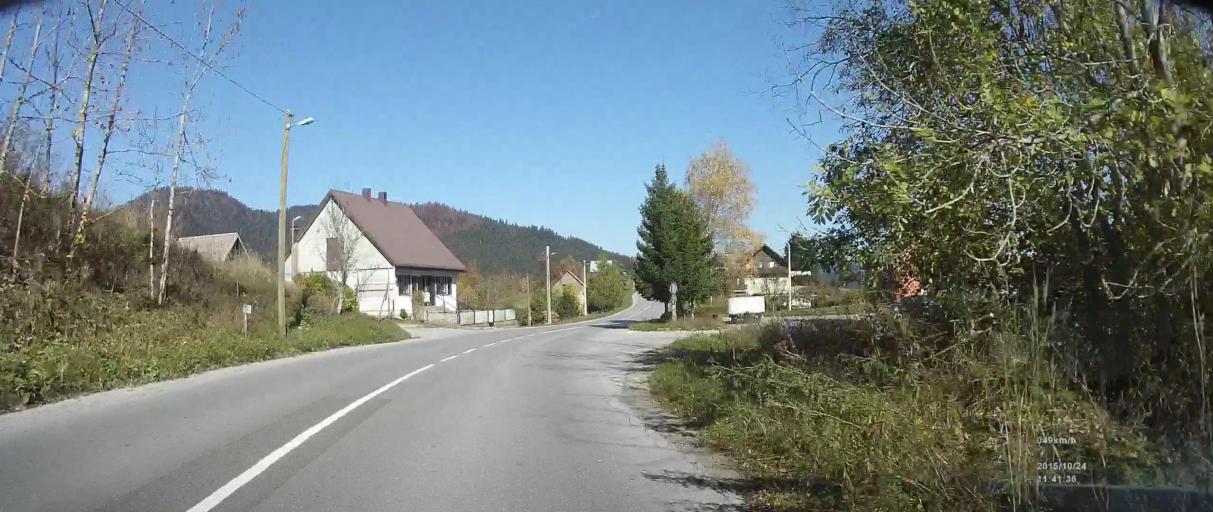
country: HR
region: Primorsko-Goranska
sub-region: Grad Delnice
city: Delnice
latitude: 45.4211
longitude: 14.7059
